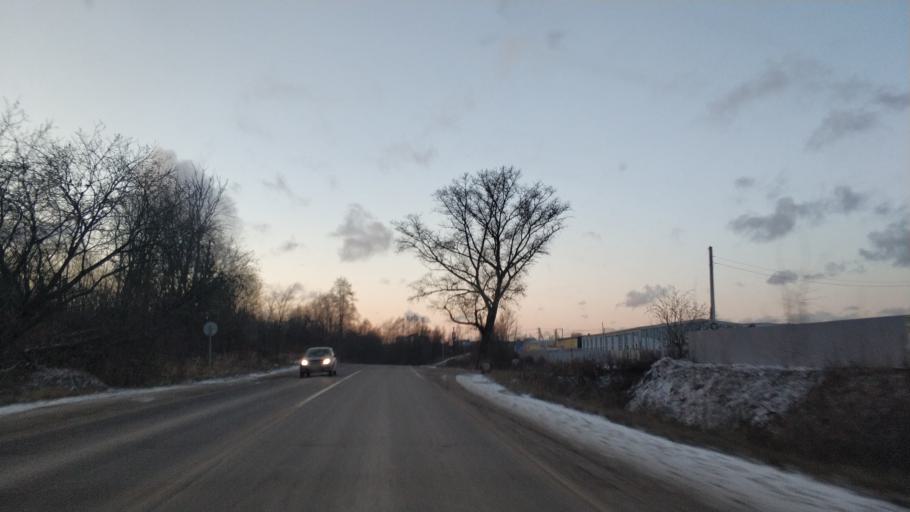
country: RU
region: St.-Petersburg
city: Pontonnyy
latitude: 59.8084
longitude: 30.6157
